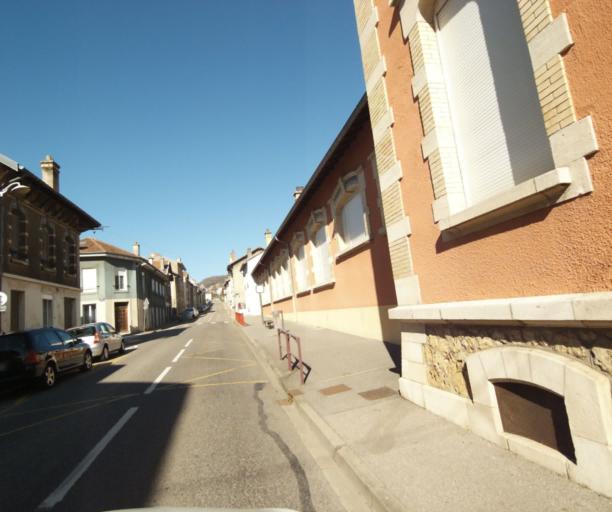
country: FR
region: Lorraine
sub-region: Departement de Meurthe-et-Moselle
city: Saint-Max
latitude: 48.7015
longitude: 6.2061
